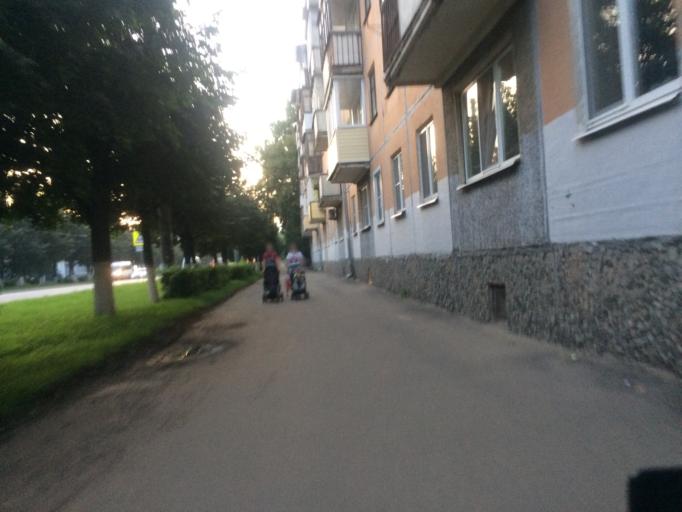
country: RU
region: Mariy-El
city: Yoshkar-Ola
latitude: 56.6350
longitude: 47.8767
